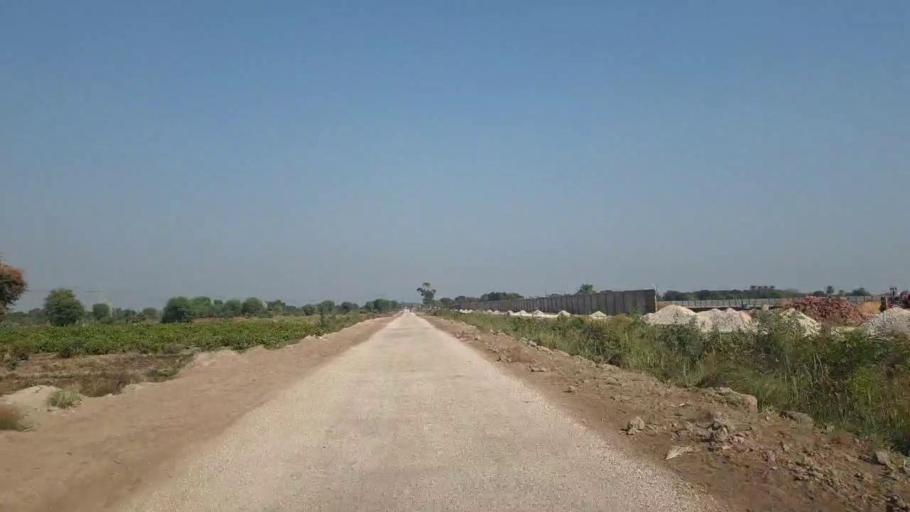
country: PK
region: Sindh
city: Hyderabad
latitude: 25.4737
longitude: 68.3883
